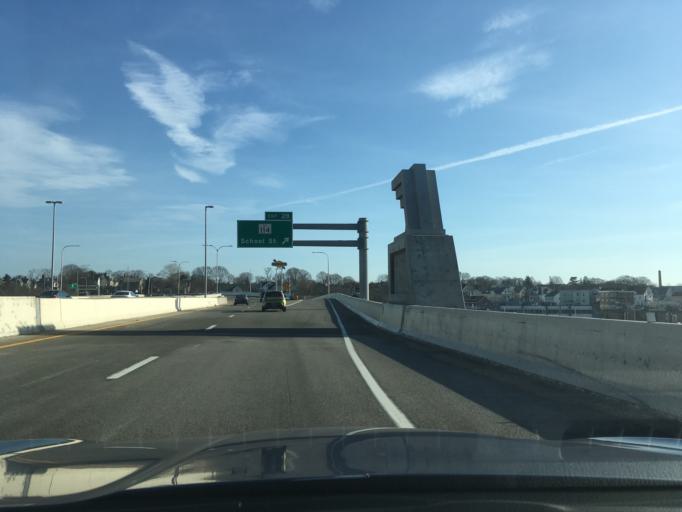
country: US
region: Rhode Island
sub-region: Providence County
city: Pawtucket
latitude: 41.8732
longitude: -71.3842
